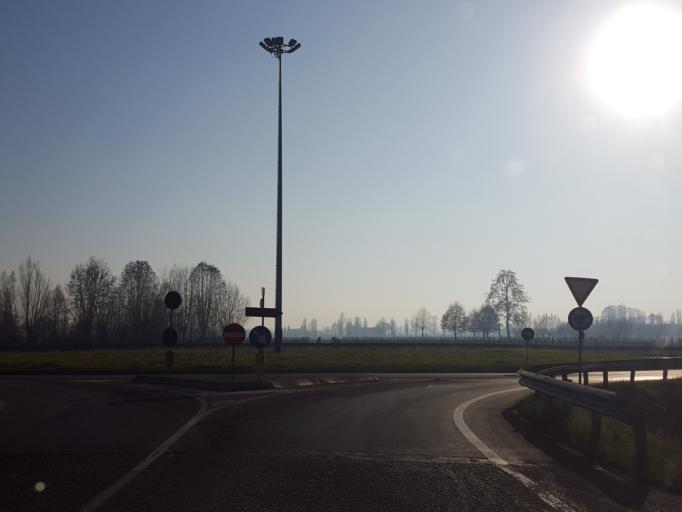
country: IT
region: Veneto
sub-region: Provincia di Vicenza
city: Torri di Quartesolo
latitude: 45.5148
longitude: 11.6381
